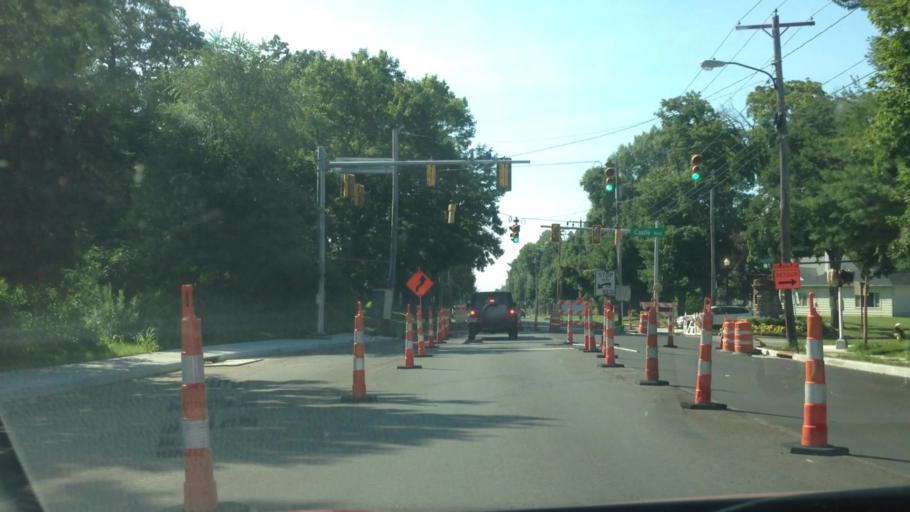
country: US
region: Ohio
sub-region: Summit County
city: Akron
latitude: 41.1057
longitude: -81.5611
